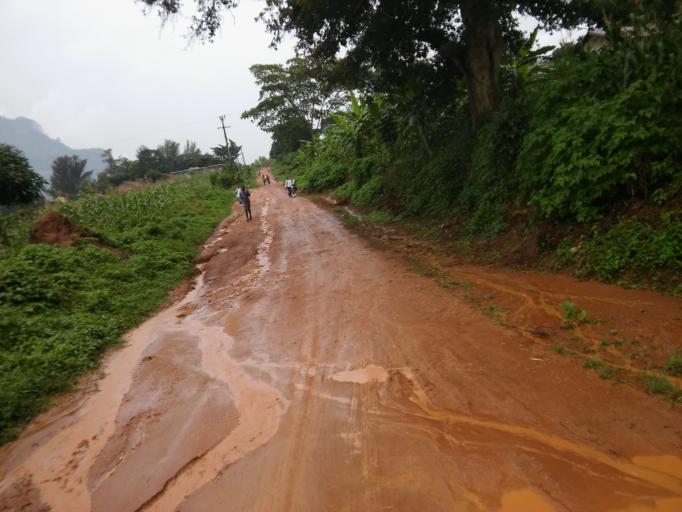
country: UG
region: Eastern Region
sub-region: Mbale District
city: Mbale
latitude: 0.9851
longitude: 34.2231
